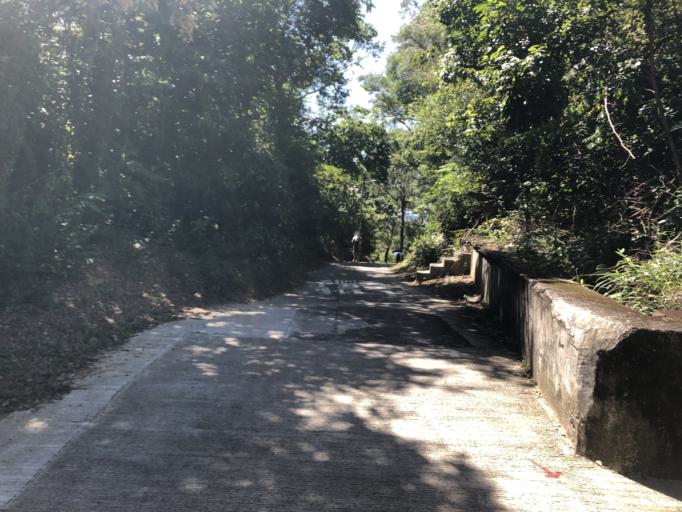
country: HK
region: Tuen Mun
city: Tuen Mun
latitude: 22.2939
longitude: 113.9740
